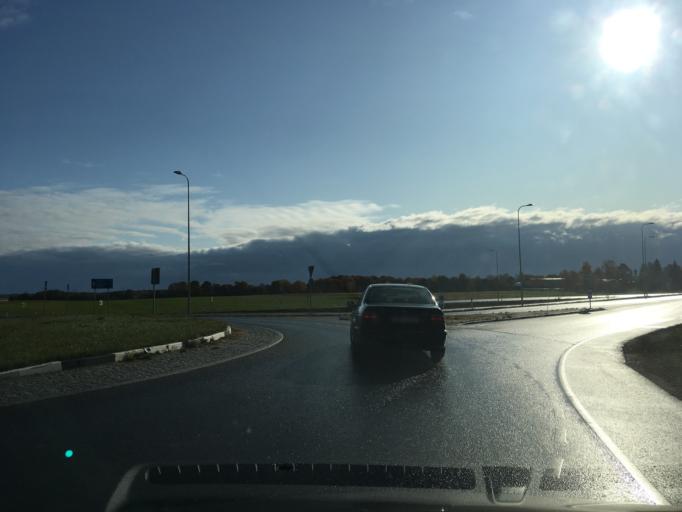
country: EE
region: Harju
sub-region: Rae vald
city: Vaida
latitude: 59.1818
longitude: 25.1182
